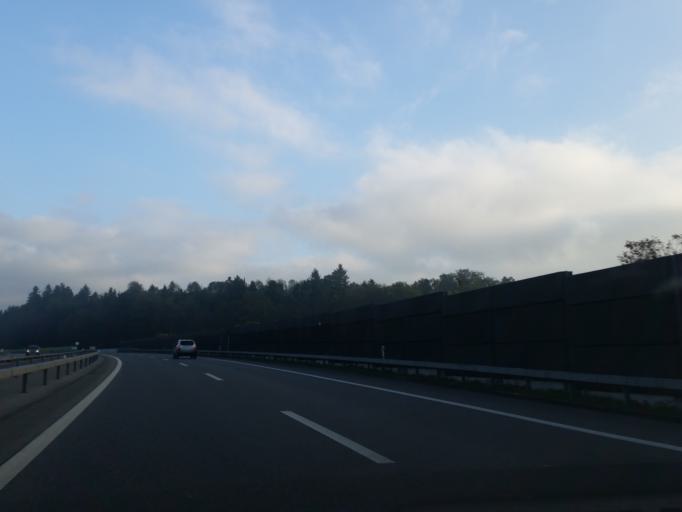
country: CH
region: Zurich
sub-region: Bezirk Affoltern
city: Knonau
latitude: 47.2082
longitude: 8.4704
